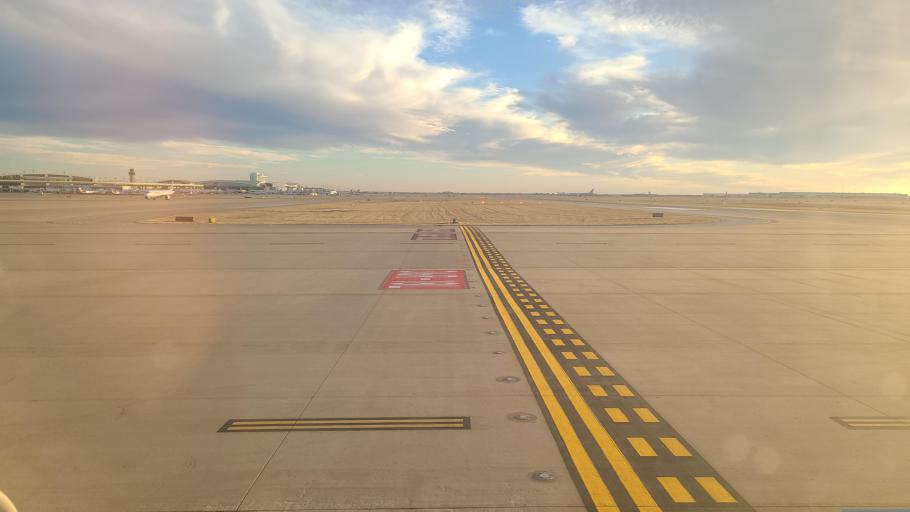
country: US
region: Texas
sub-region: Tarrant County
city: Grapevine
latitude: 32.9150
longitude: -97.0495
